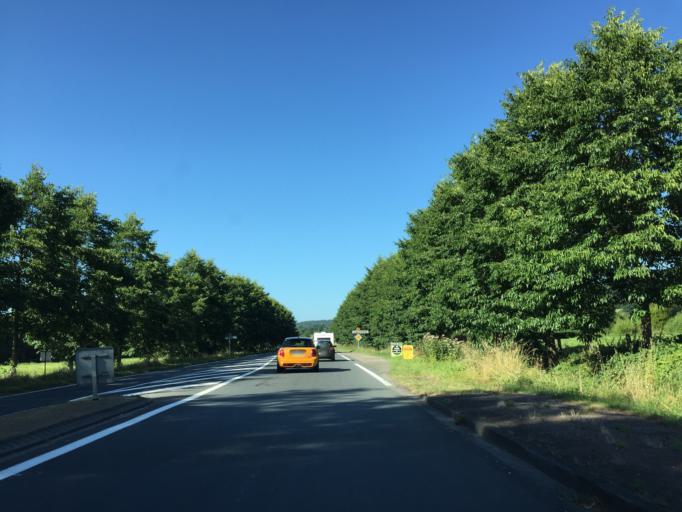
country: FR
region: Lower Normandy
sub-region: Departement du Calvados
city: Lisieux
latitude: 49.2304
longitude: 0.2185
